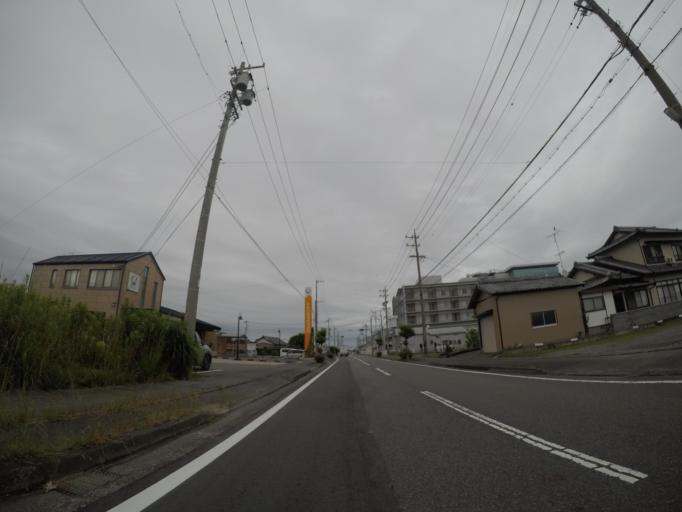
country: JP
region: Shizuoka
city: Sagara
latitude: 34.7552
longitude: 138.2364
